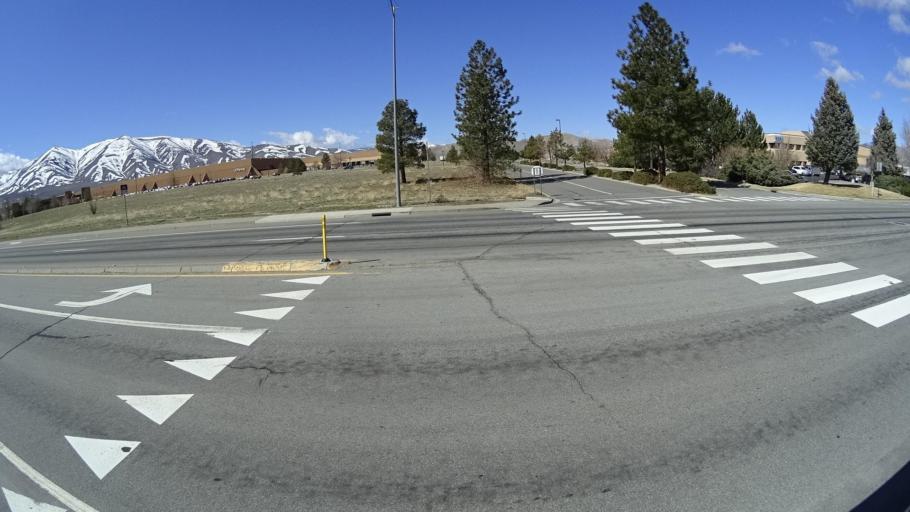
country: US
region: Nevada
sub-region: Washoe County
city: Lemmon Valley
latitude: 39.6397
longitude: -119.8818
